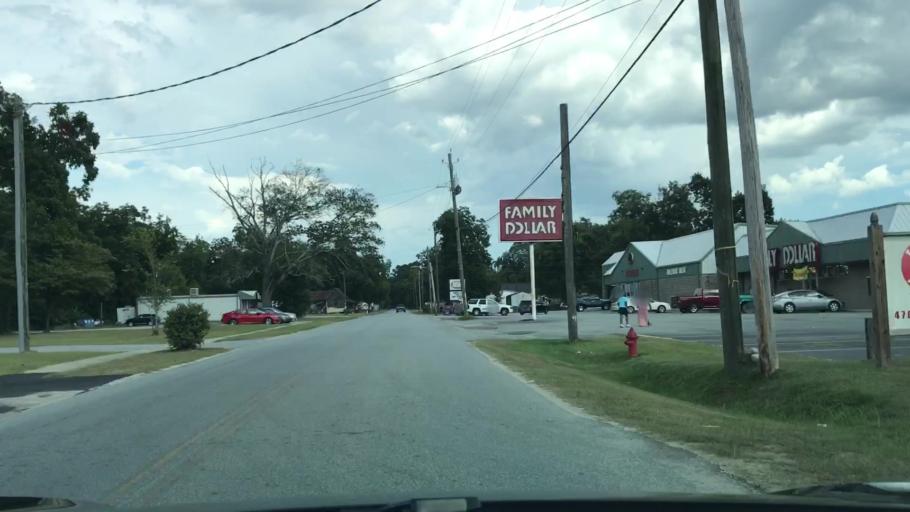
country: US
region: Georgia
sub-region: Jefferson County
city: Wadley
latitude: 32.8629
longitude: -82.4035
